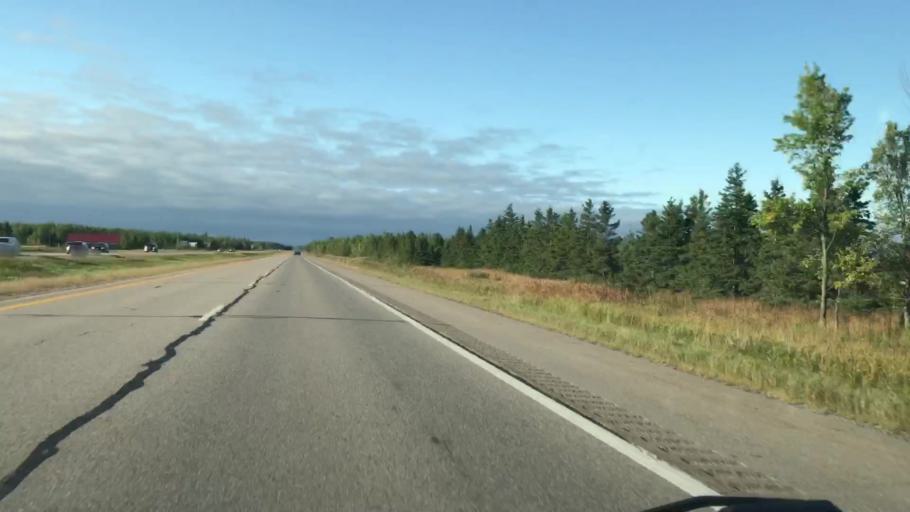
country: US
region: Michigan
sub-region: Chippewa County
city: Sault Ste. Marie
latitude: 46.4103
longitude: -84.3990
